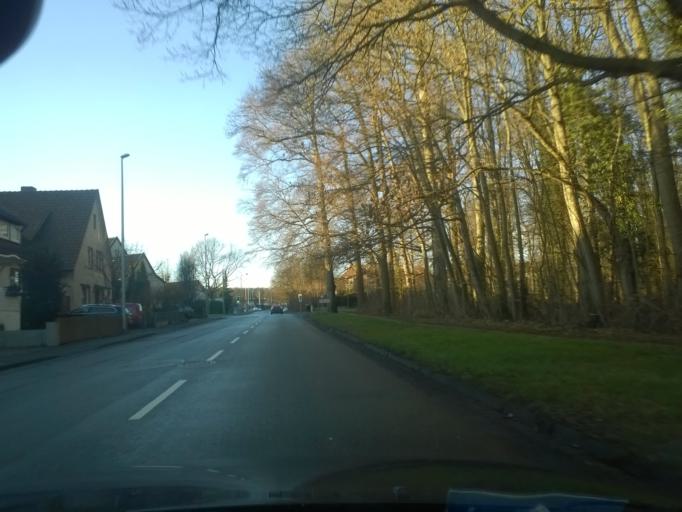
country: DE
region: Lower Saxony
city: Hildesheim
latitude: 52.1416
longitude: 9.9266
